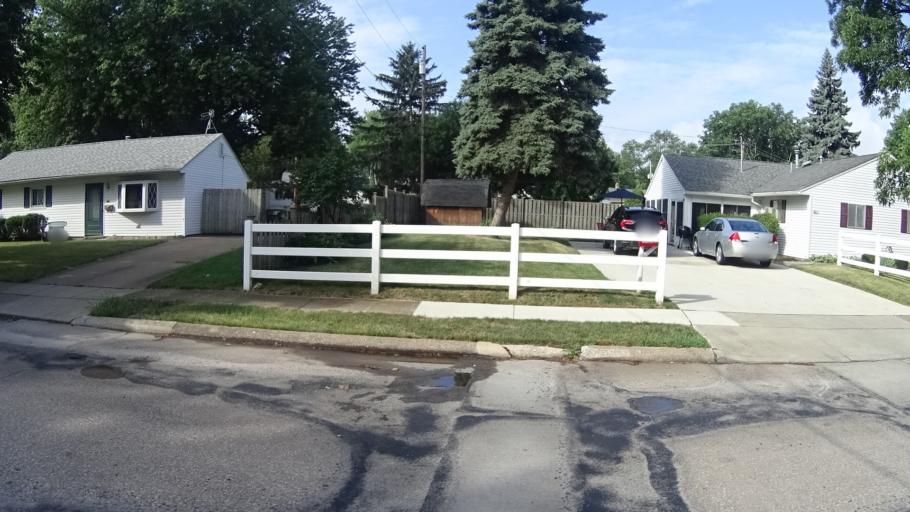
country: US
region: Ohio
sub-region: Erie County
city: Sandusky
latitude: 41.4330
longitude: -82.6770
